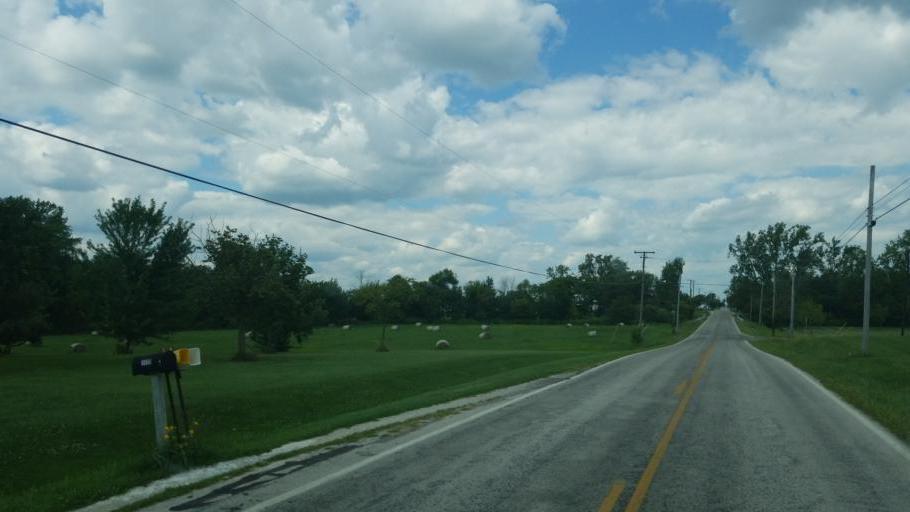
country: US
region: Ohio
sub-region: Ottawa County
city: Elmore
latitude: 41.5373
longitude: -83.2801
